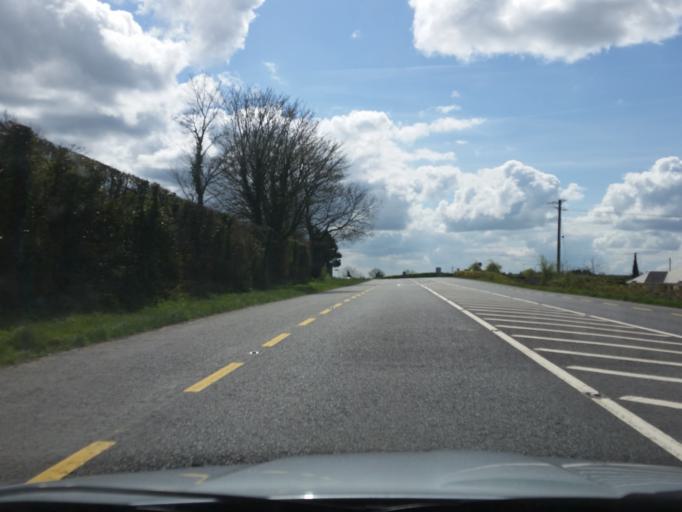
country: IE
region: Leinster
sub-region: An Mhi
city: Slane
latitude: 53.6869
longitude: -6.5416
